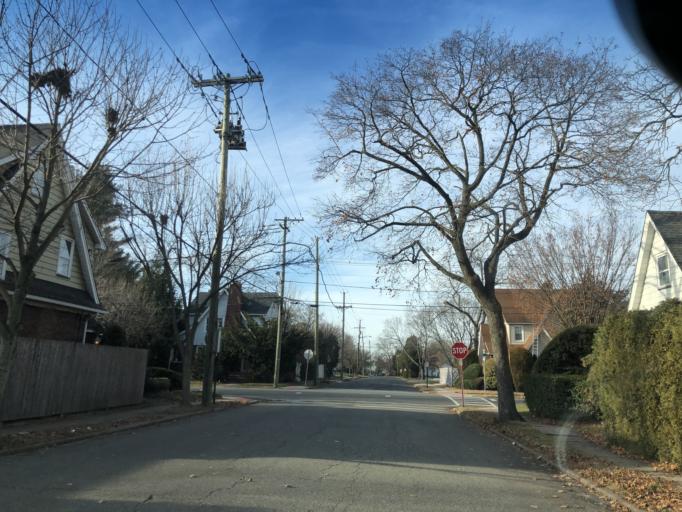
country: US
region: New Jersey
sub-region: Bergen County
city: Fair Lawn
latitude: 40.9300
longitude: -74.1257
